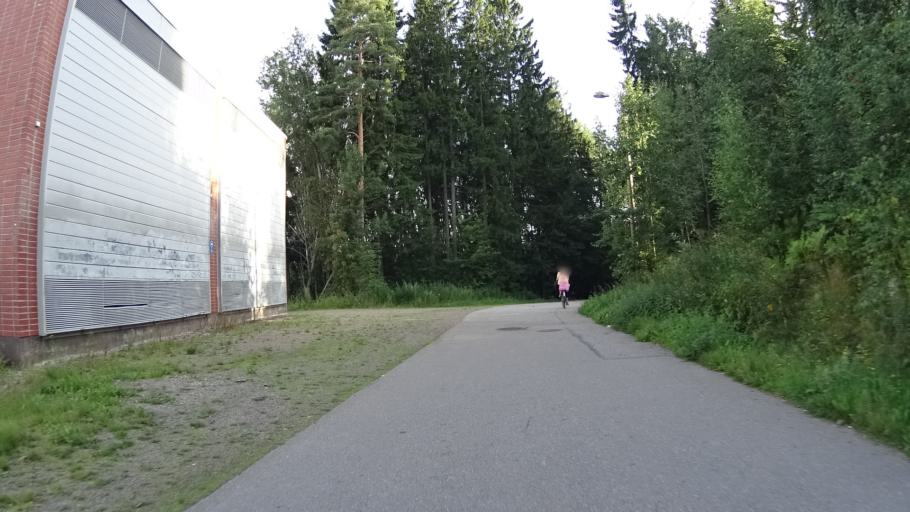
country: FI
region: Uusimaa
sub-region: Helsinki
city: Teekkarikylae
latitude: 60.2555
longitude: 24.8548
